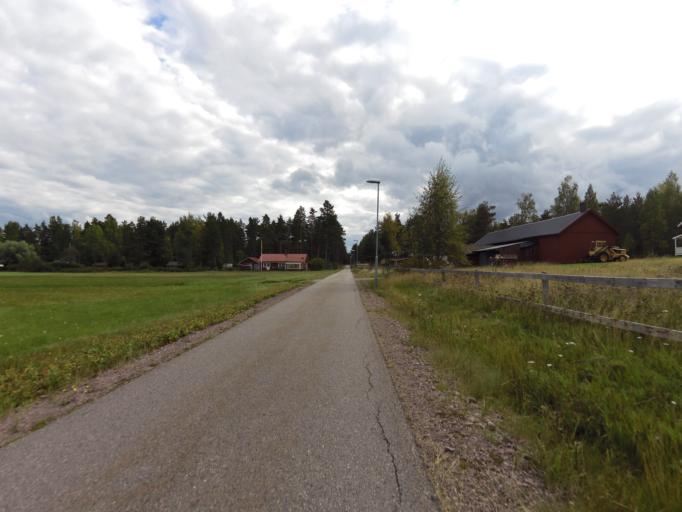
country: SE
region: Gaevleborg
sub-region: Sandvikens Kommun
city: Sandviken
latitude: 60.6849
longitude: 16.8160
